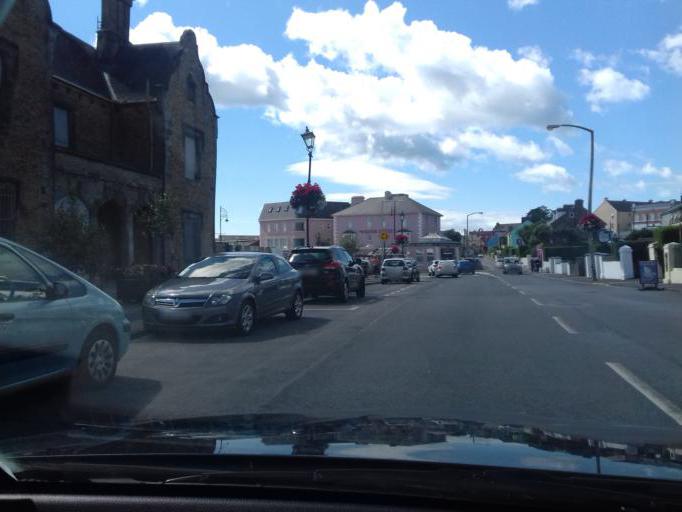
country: IE
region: Munster
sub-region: Waterford
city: Tra Mhor
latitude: 52.1621
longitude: -7.1487
